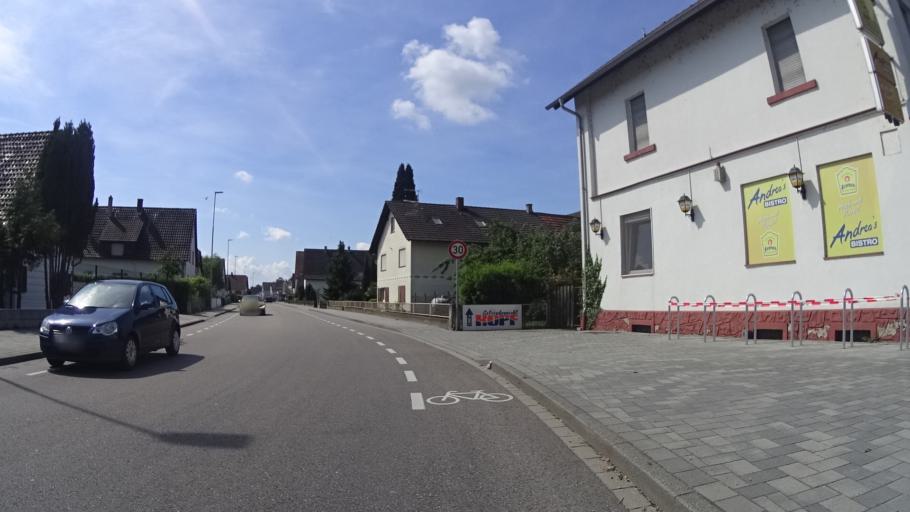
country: DE
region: Baden-Wuerttemberg
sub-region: Freiburg Region
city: Kehl
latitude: 48.5092
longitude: 7.8200
